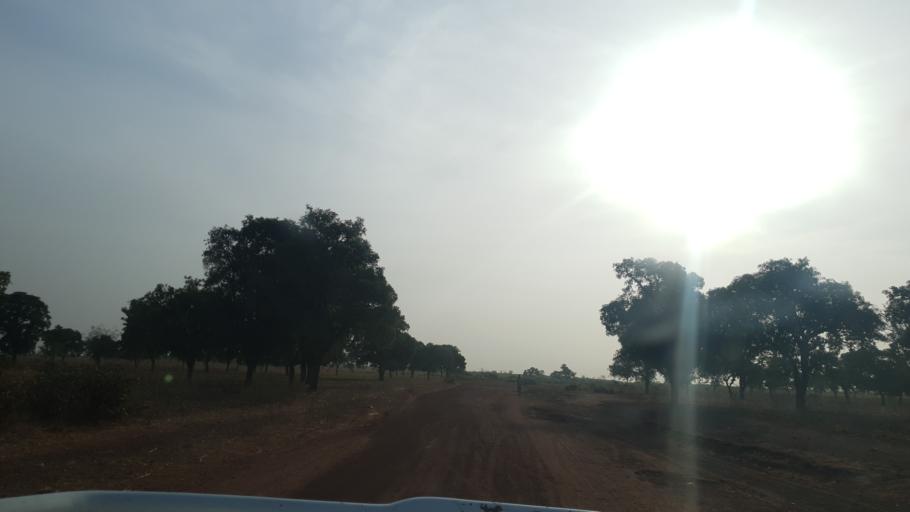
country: ML
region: Koulikoro
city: Dioila
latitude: 12.7698
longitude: -6.9279
